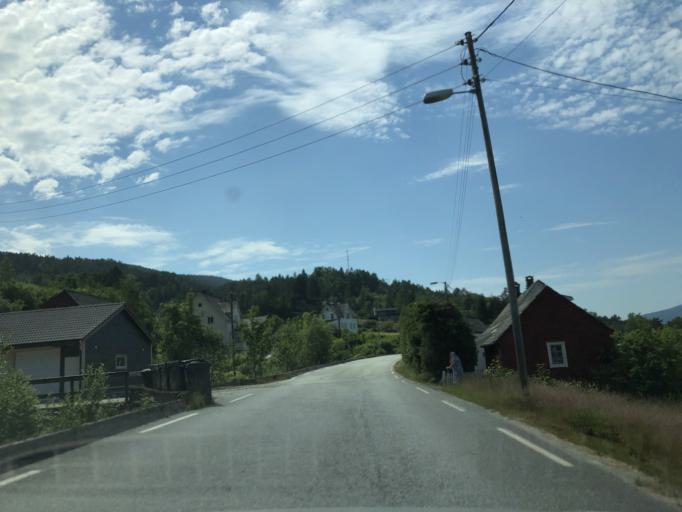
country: NO
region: Hordaland
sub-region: Jondal
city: Jondal
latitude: 60.3153
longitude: 6.3225
